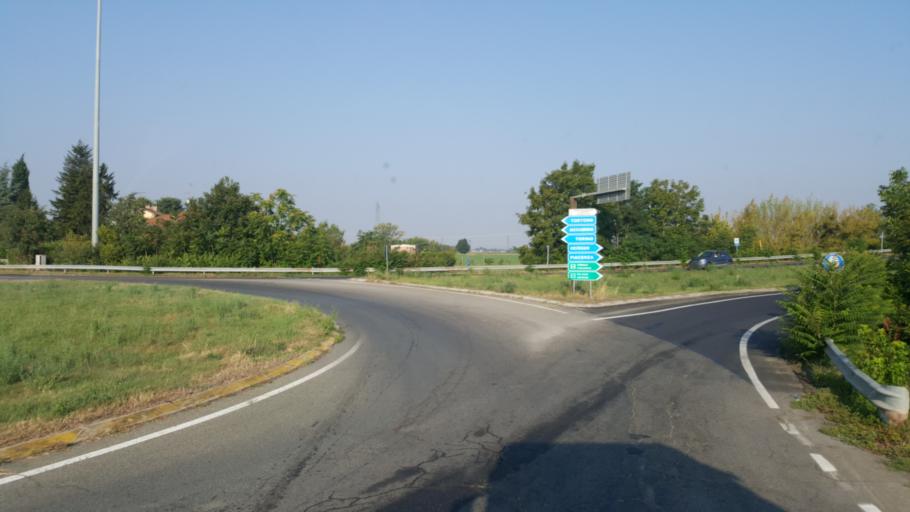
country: IT
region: Lombardy
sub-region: Provincia di Pavia
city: Voghera
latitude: 44.9796
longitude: 8.9735
